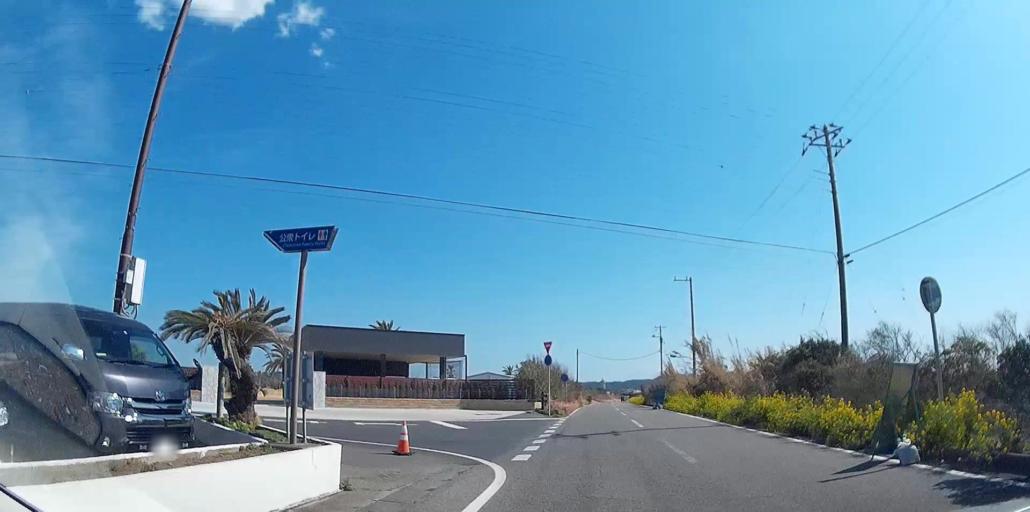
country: JP
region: Chiba
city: Tateyama
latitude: 34.9455
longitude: 139.8146
